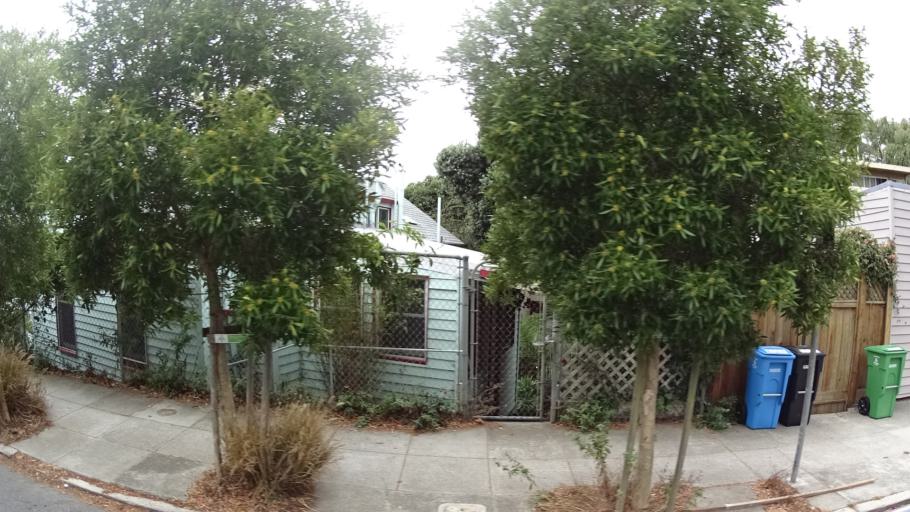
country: US
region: California
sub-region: San Mateo County
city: Daly City
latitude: 37.7361
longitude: -122.4340
